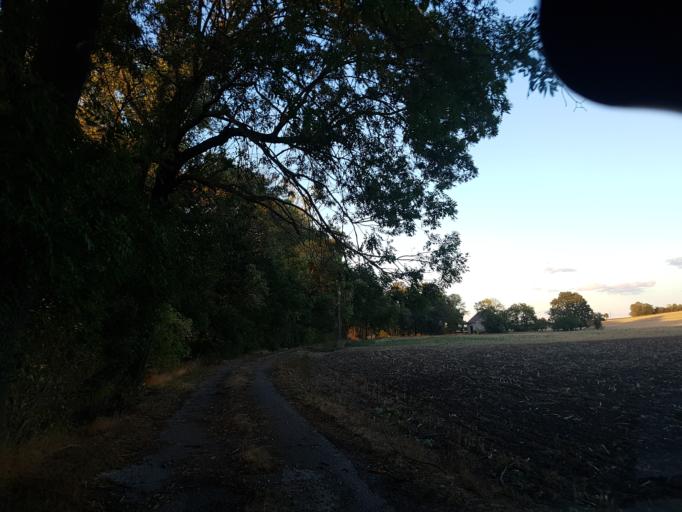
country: DE
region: Saxony
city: Oschatz
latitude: 51.2945
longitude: 13.1606
